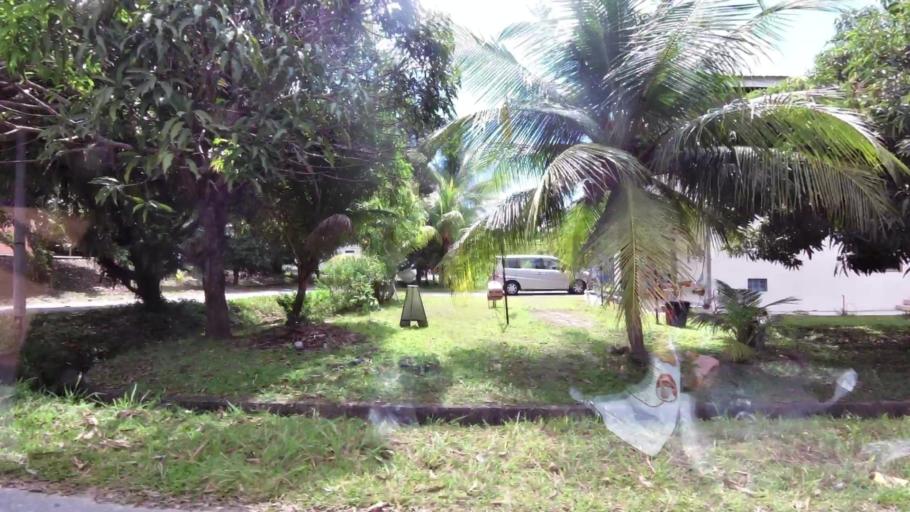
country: BN
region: Brunei and Muara
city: Bandar Seri Begawan
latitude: 4.9859
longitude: 114.9442
